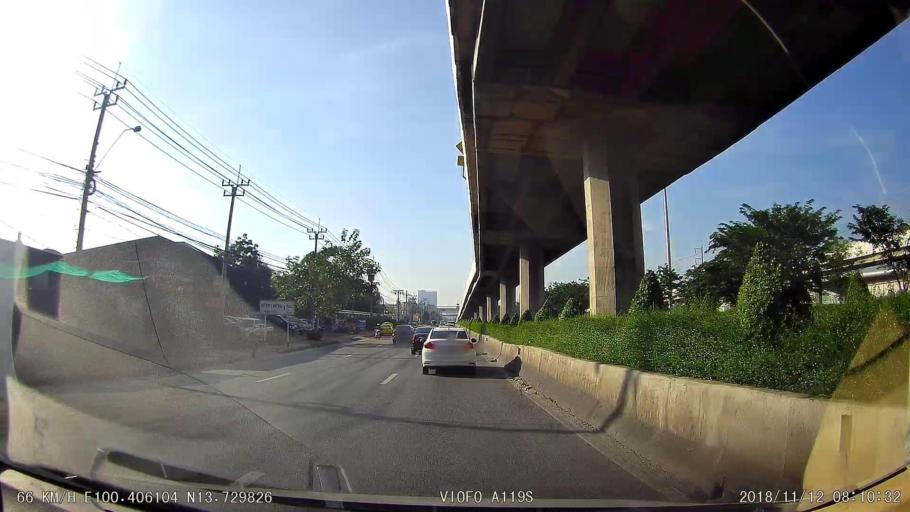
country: TH
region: Bangkok
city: Phasi Charoen
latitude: 13.7296
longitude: 100.4061
